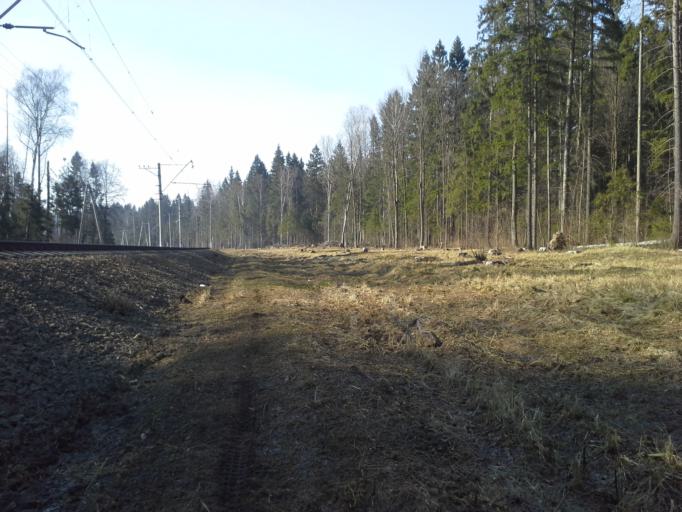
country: RU
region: Moscow
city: Tolstopal'tsevo
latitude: 55.6177
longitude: 37.2432
